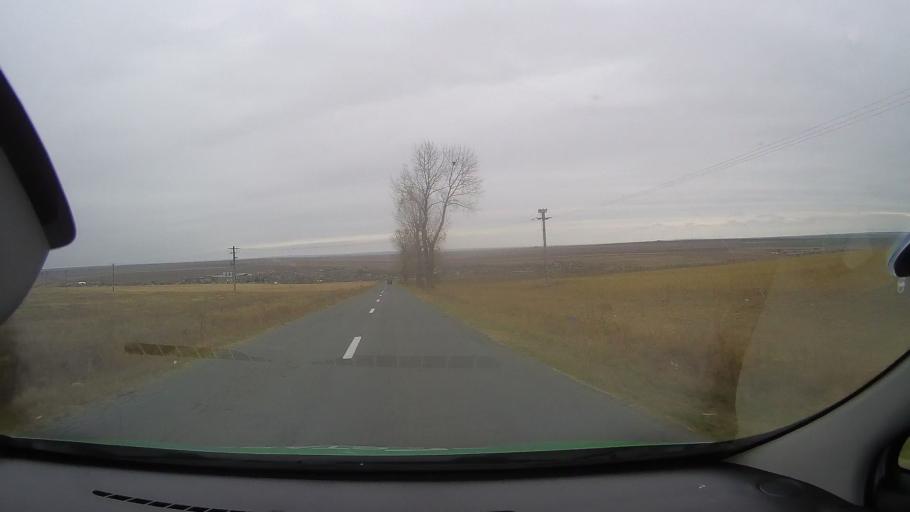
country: RO
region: Constanta
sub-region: Comuna Pantelimon
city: Pantelimon
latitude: 44.5918
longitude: 28.3208
